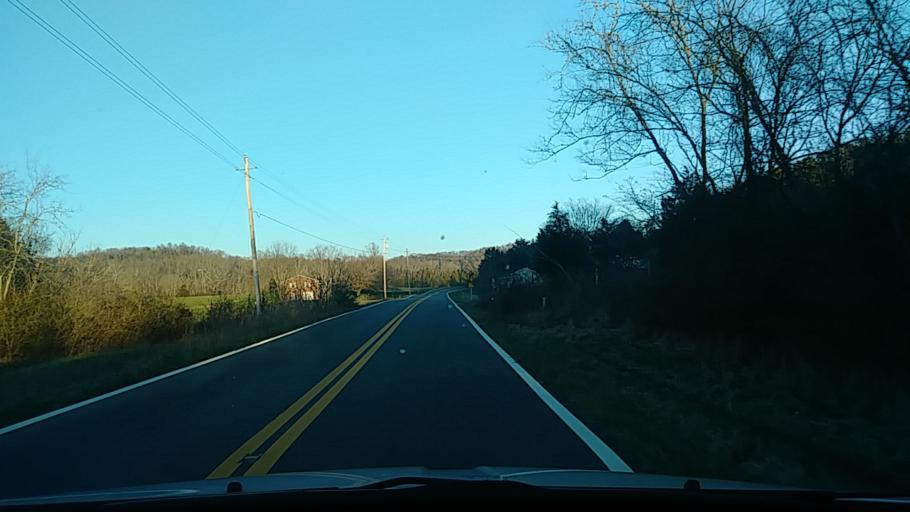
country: US
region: Tennessee
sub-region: Greene County
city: Mosheim
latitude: 36.1246
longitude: -83.0571
